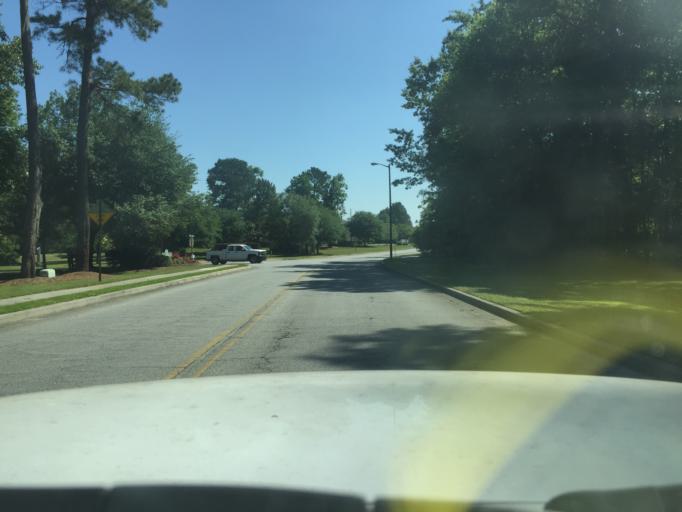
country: US
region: Georgia
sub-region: Chatham County
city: Georgetown
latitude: 32.0042
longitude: -81.2558
